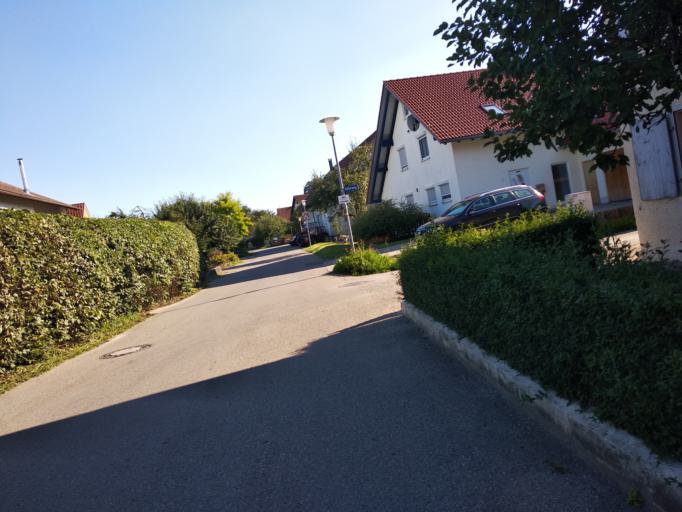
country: DE
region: Baden-Wuerttemberg
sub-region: Tuebingen Region
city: Leutkirch im Allgau
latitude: 47.7768
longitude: 10.0413
